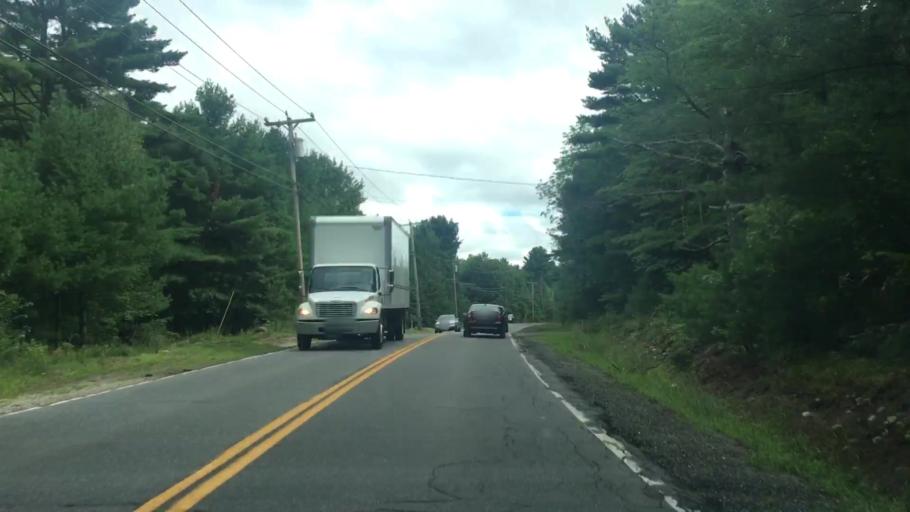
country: US
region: Maine
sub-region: York County
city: Lake Arrowhead
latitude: 43.6141
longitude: -70.7196
